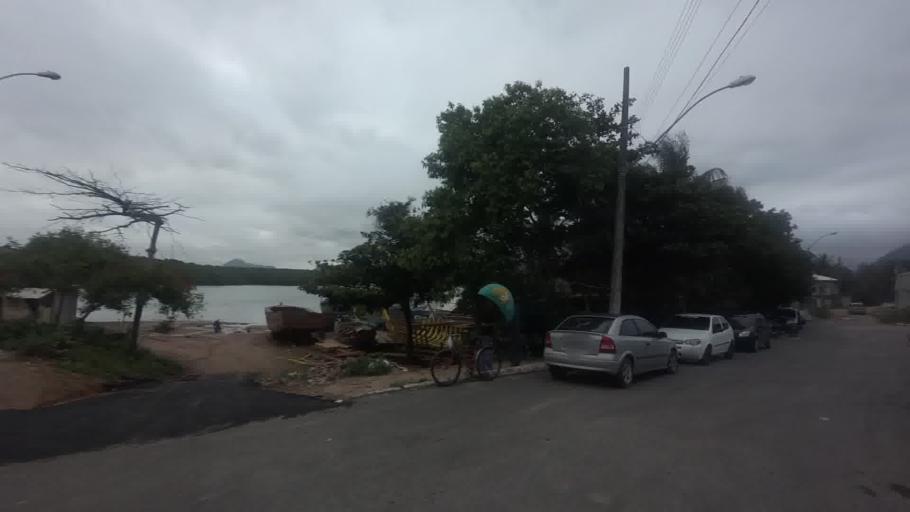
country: BR
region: Espirito Santo
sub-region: Guarapari
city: Guarapari
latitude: -20.6658
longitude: -40.5133
